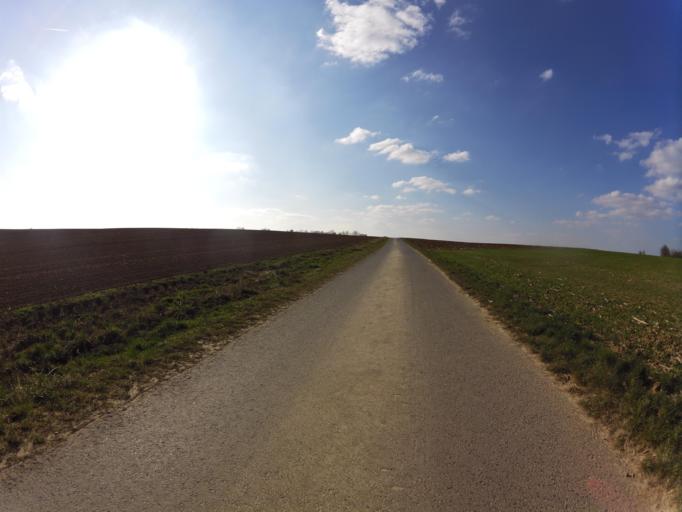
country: DE
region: Bavaria
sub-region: Regierungsbezirk Unterfranken
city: Prosselsheim
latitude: 49.8410
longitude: 10.1279
